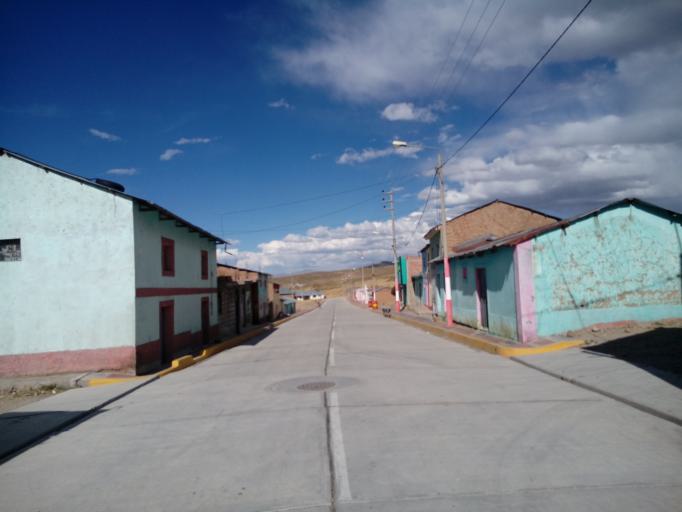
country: PE
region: Puno
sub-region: El Collao
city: Mazo Cruz
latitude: -16.7618
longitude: -69.8549
